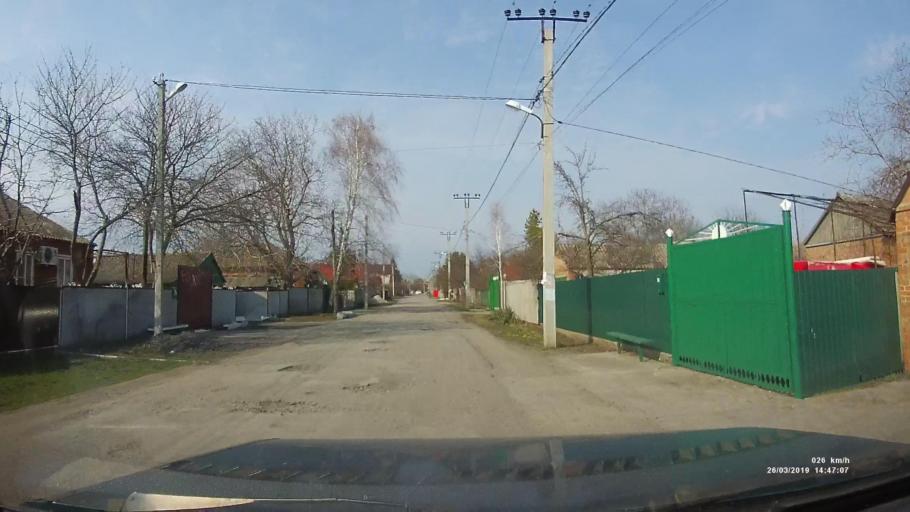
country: RU
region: Rostov
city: Novobessergenovka
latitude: 47.1894
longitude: 38.8595
